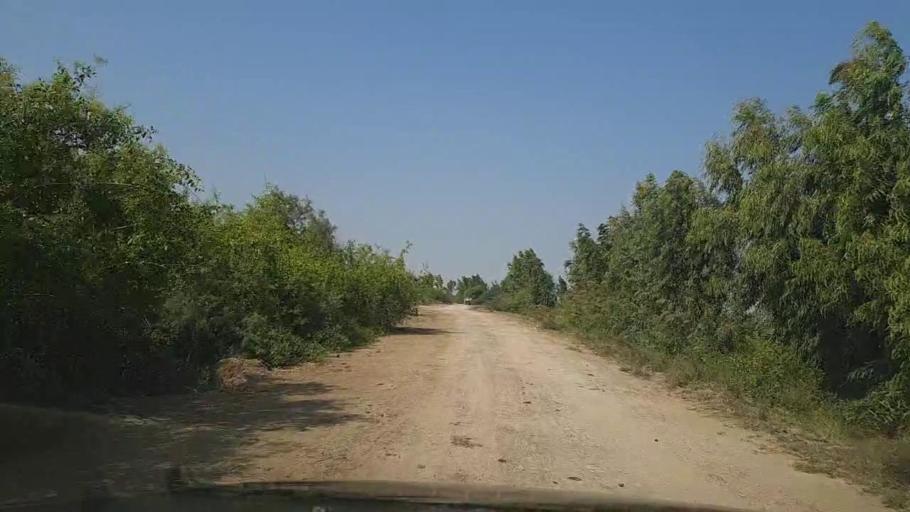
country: PK
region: Sindh
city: Thatta
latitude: 24.6431
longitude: 67.8073
